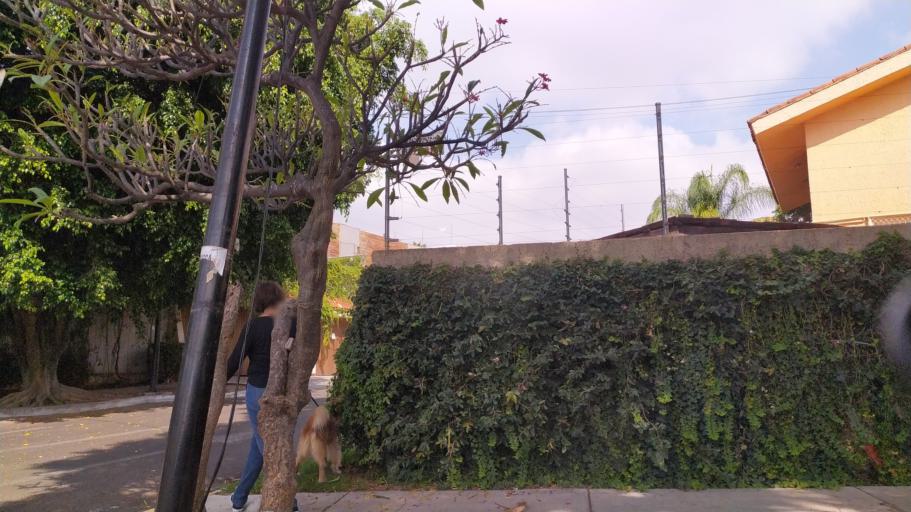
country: MX
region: Jalisco
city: Zapopan2
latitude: 20.6926
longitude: -103.4127
